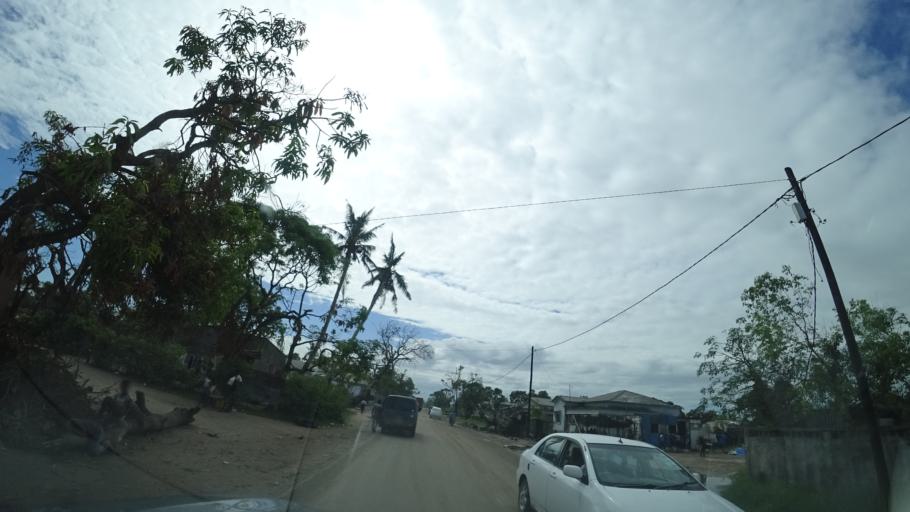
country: MZ
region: Sofala
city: Beira
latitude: -19.7706
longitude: 34.8689
